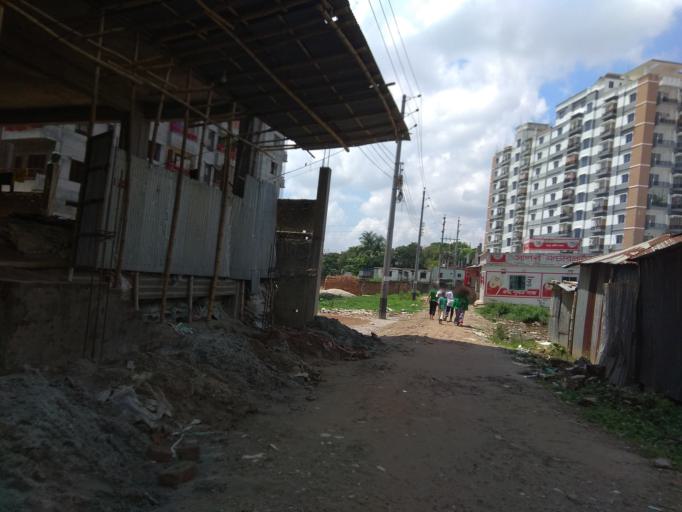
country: BD
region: Dhaka
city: Tungi
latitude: 23.8302
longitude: 90.3878
